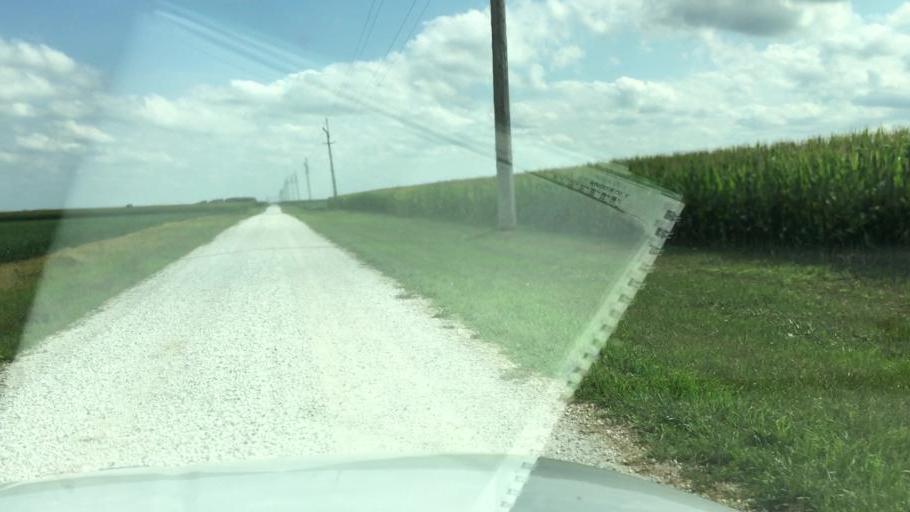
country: US
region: Illinois
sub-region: Hancock County
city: Carthage
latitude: 40.4148
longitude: -91.1784
